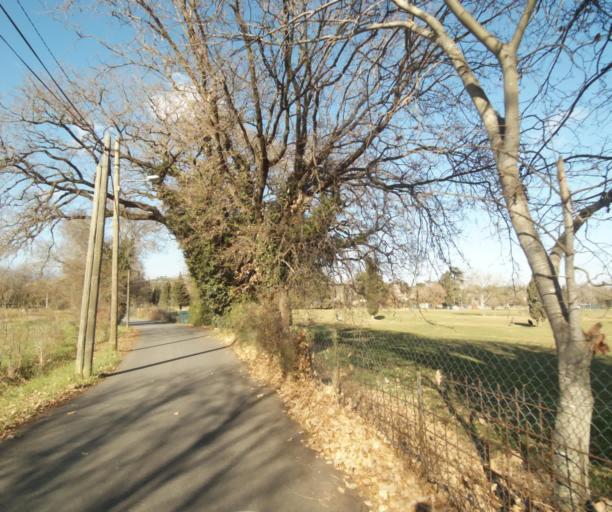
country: FR
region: Provence-Alpes-Cote d'Azur
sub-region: Departement des Alpes-Maritimes
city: Biot
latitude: 43.6156
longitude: 7.1035
